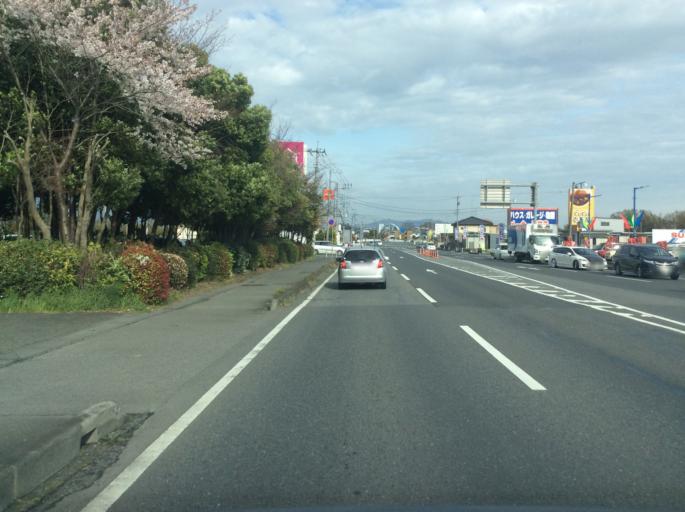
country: JP
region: Ibaraki
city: Ishige
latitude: 36.1879
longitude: 139.9893
